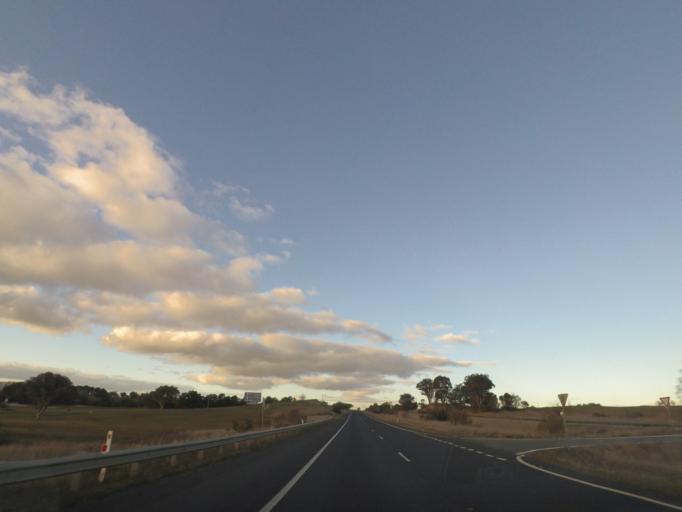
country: AU
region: New South Wales
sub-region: Yass Valley
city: Yass
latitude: -34.7692
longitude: 148.7487
